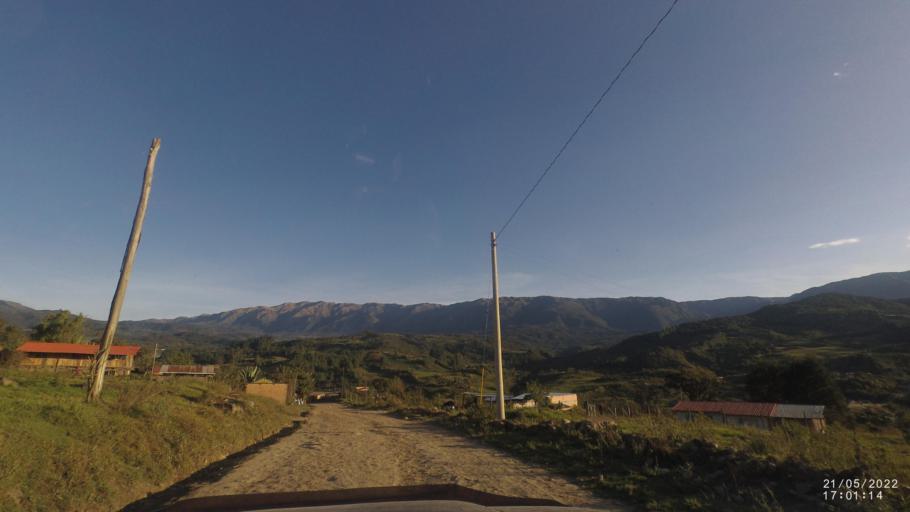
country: BO
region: Cochabamba
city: Colomi
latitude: -17.1278
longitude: -65.9362
